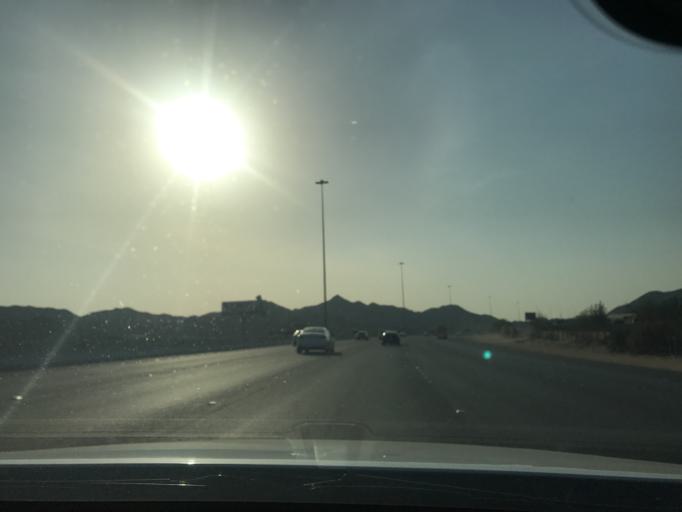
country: SA
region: Makkah
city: Jeddah
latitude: 21.3905
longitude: 39.4163
